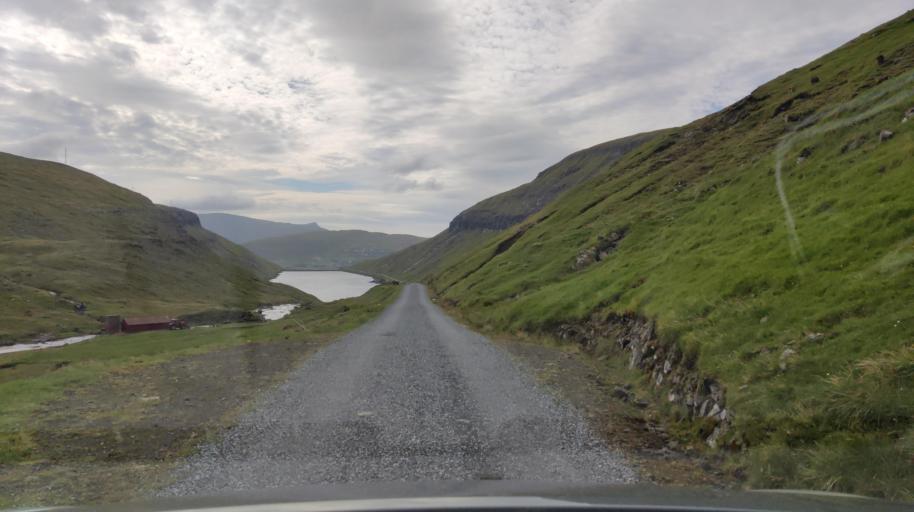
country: FO
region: Streymoy
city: Vestmanna
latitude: 62.1544
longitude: -7.0945
